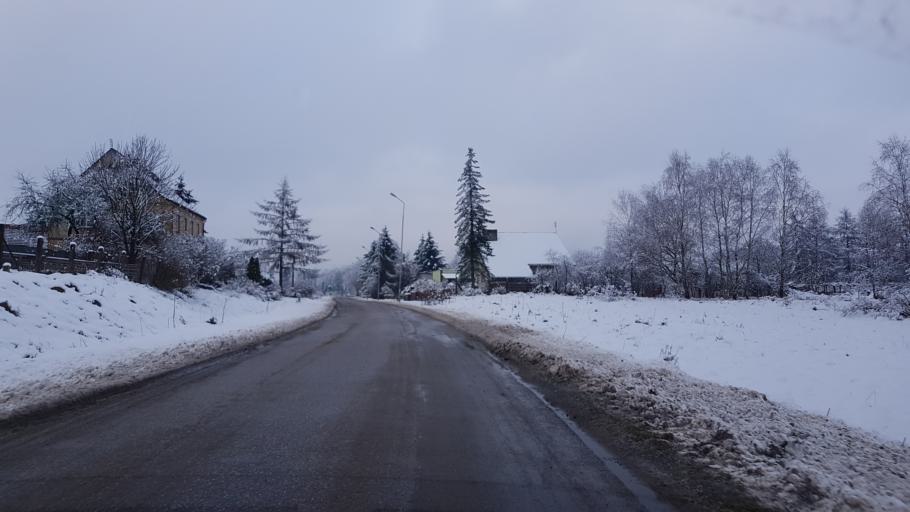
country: PL
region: West Pomeranian Voivodeship
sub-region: Powiat drawski
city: Zlocieniec
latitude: 53.5212
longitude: 16.0063
